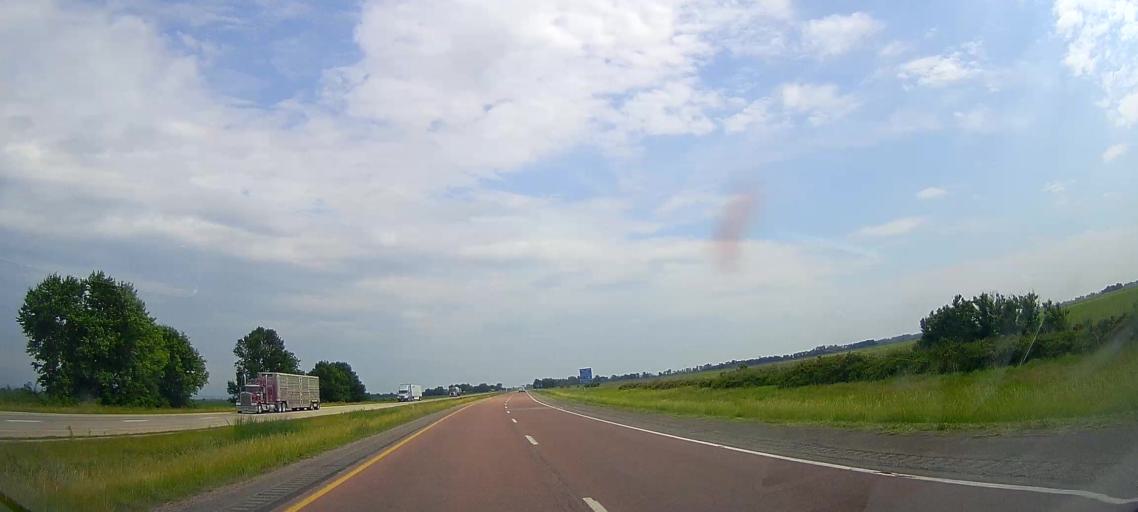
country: US
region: Iowa
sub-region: Monona County
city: Onawa
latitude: 42.0079
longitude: -96.1175
